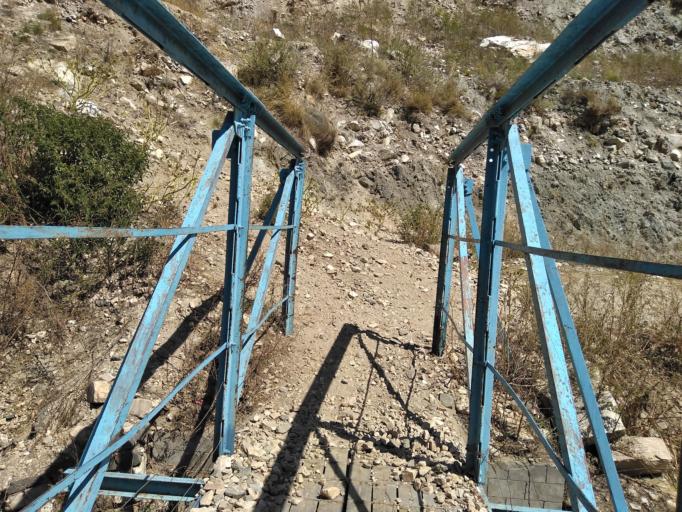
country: NP
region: Mid Western
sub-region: Karnali Zone
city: Jumla
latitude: 28.9379
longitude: 82.9041
